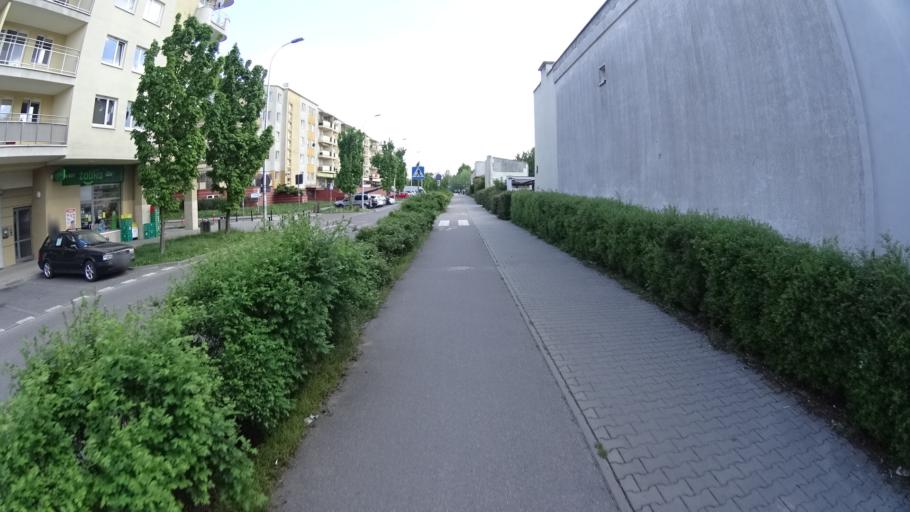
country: PL
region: Masovian Voivodeship
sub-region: Warszawa
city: Mokotow
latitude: 52.2118
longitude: 21.0586
